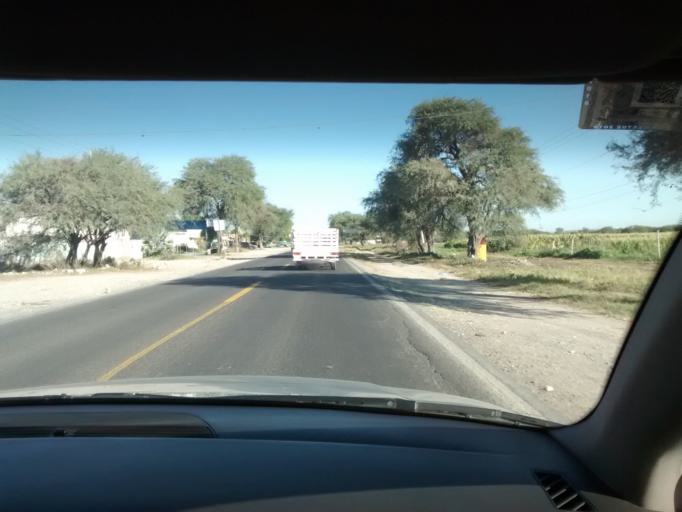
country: MX
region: Puebla
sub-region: Santiago Miahuatlan
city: San Jose Monte Chiquito
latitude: 18.5040
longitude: -97.4818
